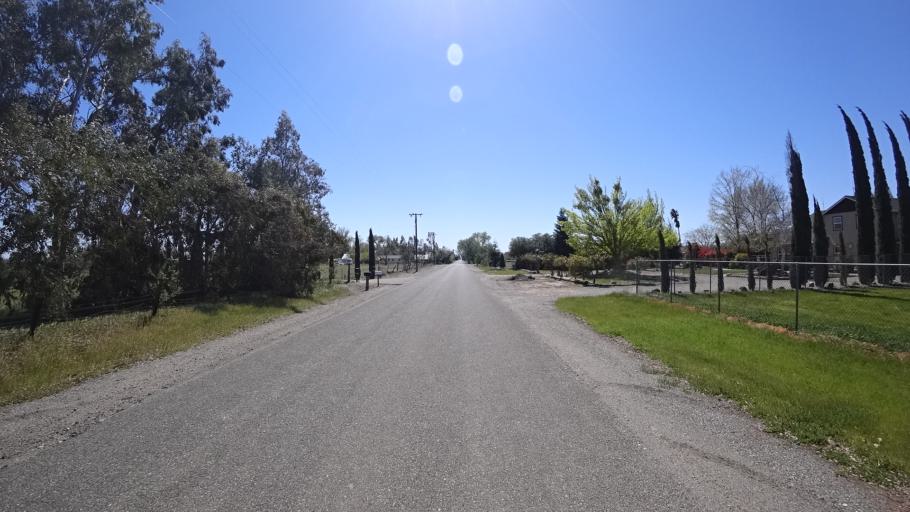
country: US
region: California
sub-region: Glenn County
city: Orland
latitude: 39.7782
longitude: -122.2386
